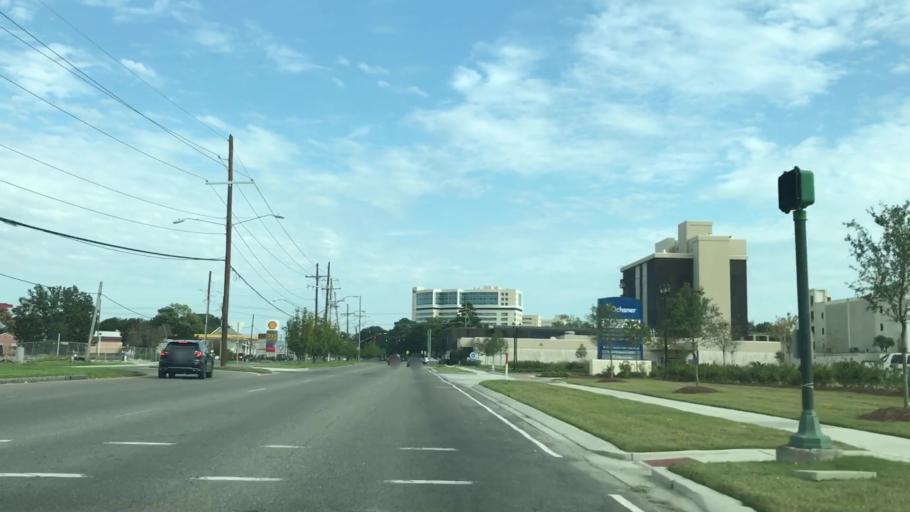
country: US
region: Louisiana
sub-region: Jefferson Parish
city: Jefferson
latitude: 29.9629
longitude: -90.1547
